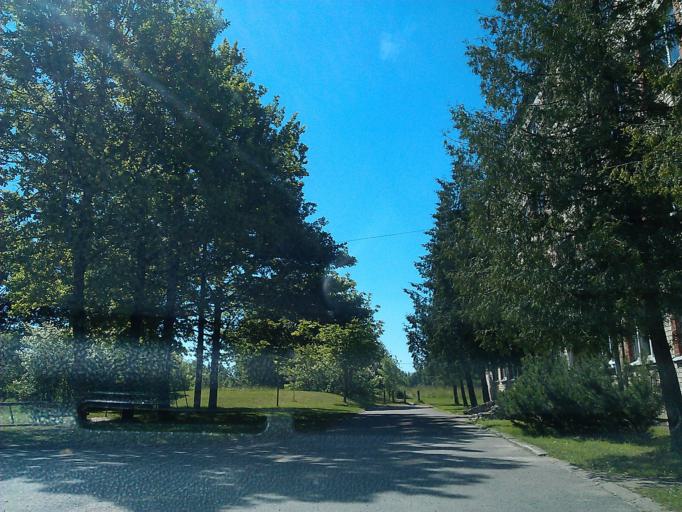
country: LV
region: Vilanu
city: Vilani
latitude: 56.5446
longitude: 26.9330
